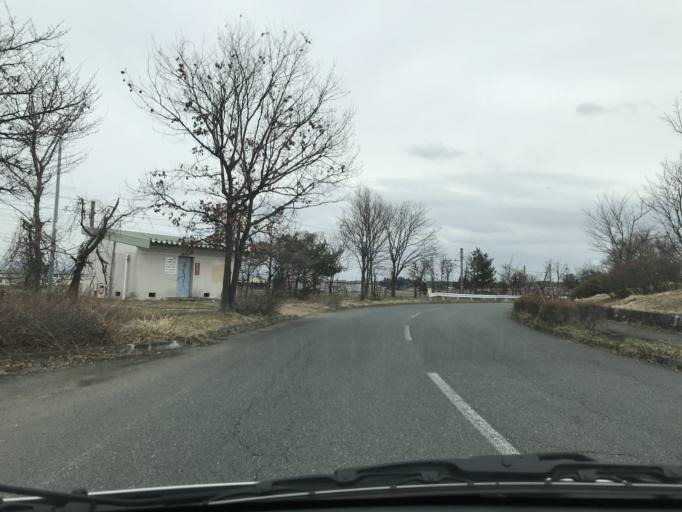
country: JP
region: Iwate
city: Kitakami
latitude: 39.2540
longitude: 141.1051
